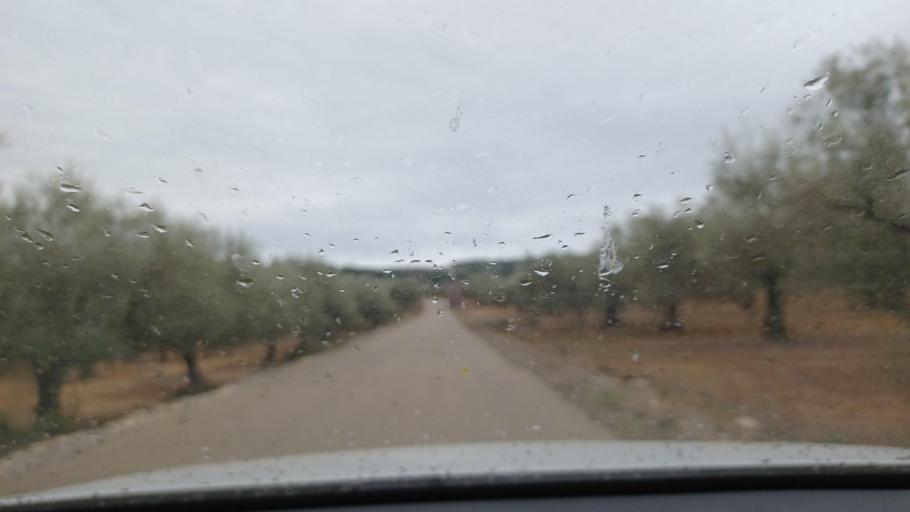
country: ES
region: Valencia
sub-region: Provincia de Castello
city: Traiguera
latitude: 40.5139
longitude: 0.2923
